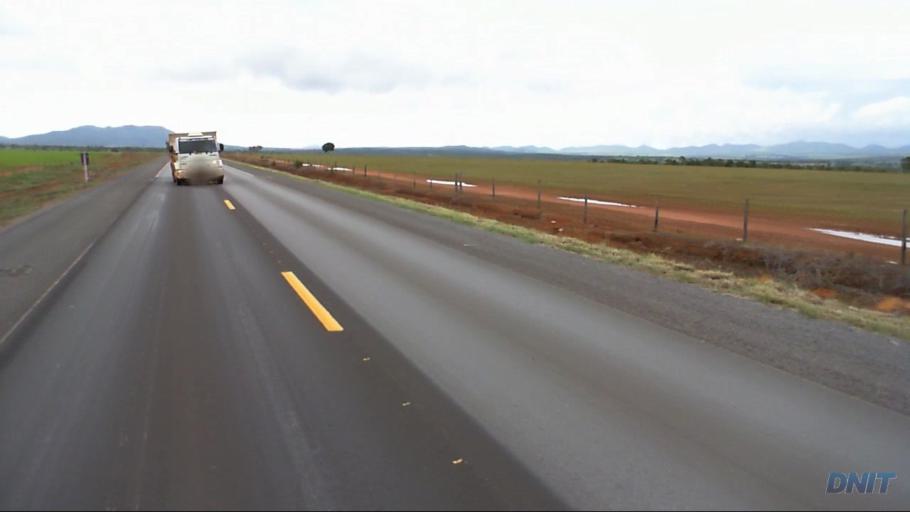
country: BR
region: Goias
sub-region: Padre Bernardo
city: Padre Bernardo
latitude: -15.2194
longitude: -48.6341
